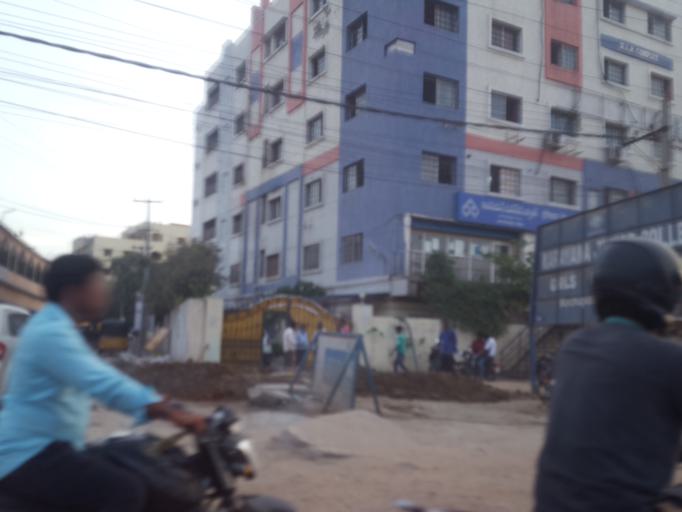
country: IN
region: Telangana
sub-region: Rangareddi
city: Kukatpalli
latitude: 17.5405
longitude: 78.3650
